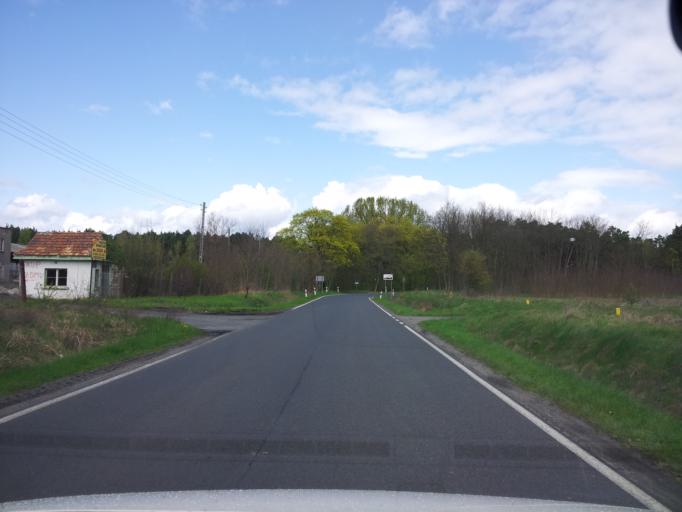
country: PL
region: Lubusz
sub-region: Powiat zielonogorski
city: Ochla
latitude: 51.8685
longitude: 15.5086
